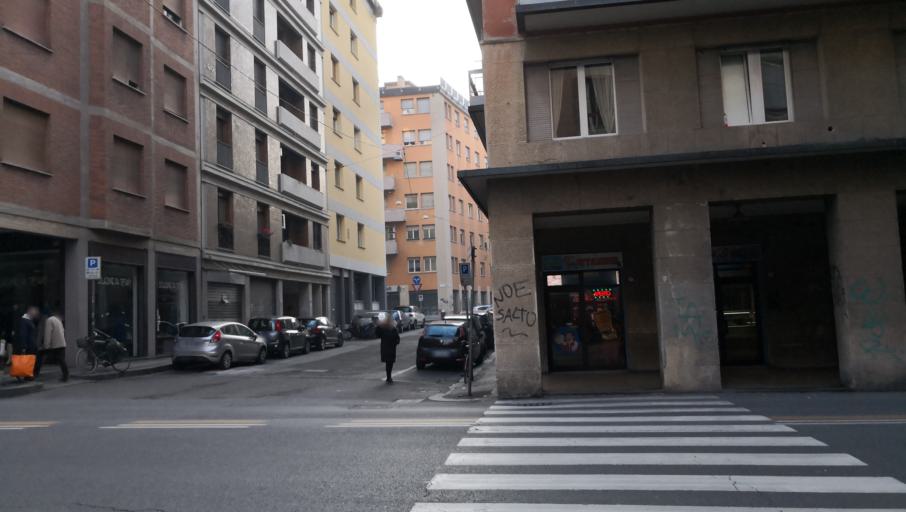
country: IT
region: Emilia-Romagna
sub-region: Provincia di Bologna
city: Bologna
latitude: 44.4996
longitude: 11.3350
